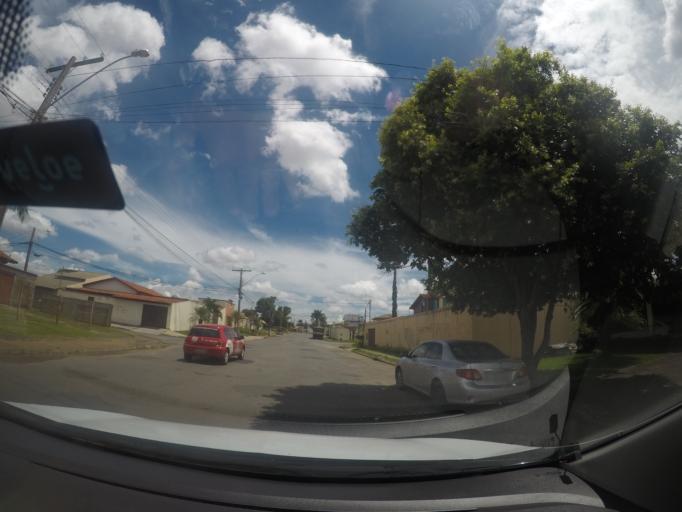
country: BR
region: Goias
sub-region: Goiania
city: Goiania
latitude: -16.6821
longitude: -49.3169
